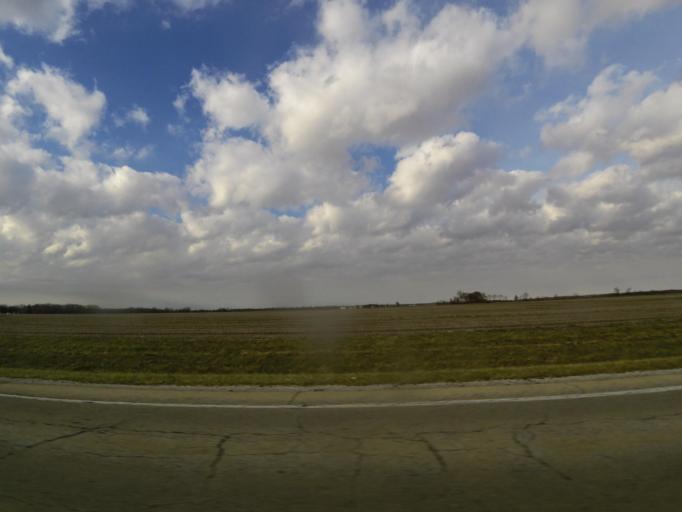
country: US
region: Illinois
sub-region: Fayette County
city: Ramsey
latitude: 39.2088
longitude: -89.1009
